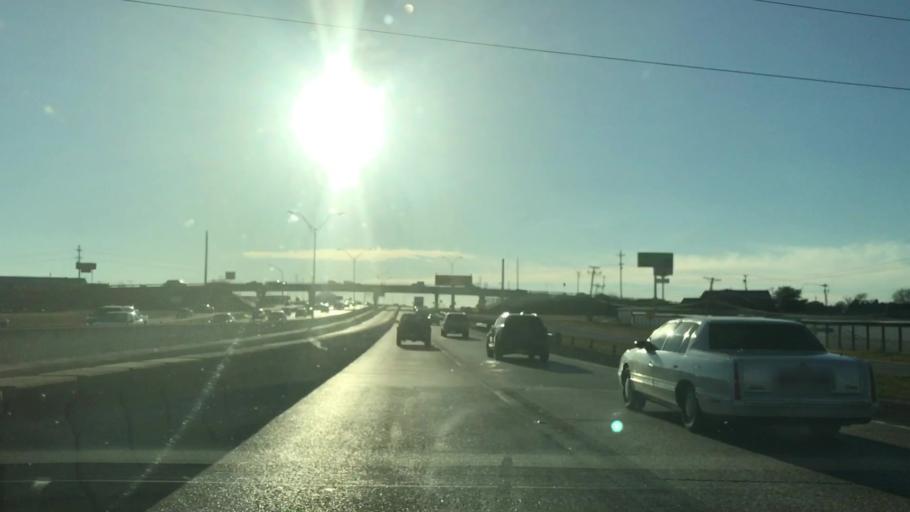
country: US
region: Texas
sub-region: Dallas County
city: Mesquite
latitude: 32.8192
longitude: -96.6369
